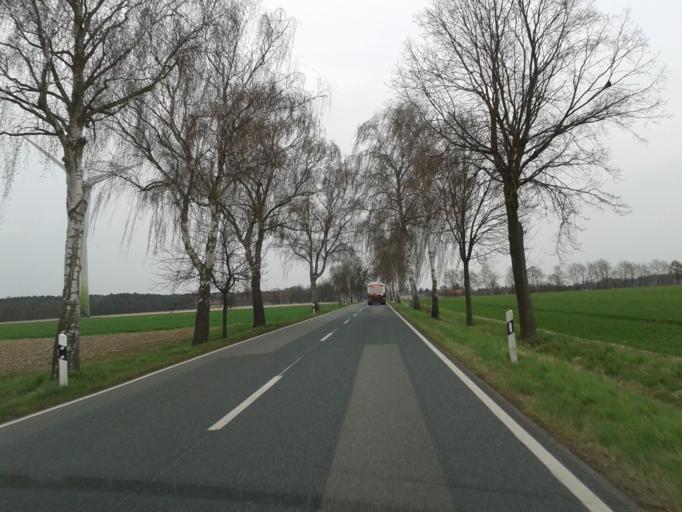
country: DE
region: Lower Saxony
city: Trebel
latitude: 52.9114
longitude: 11.3067
